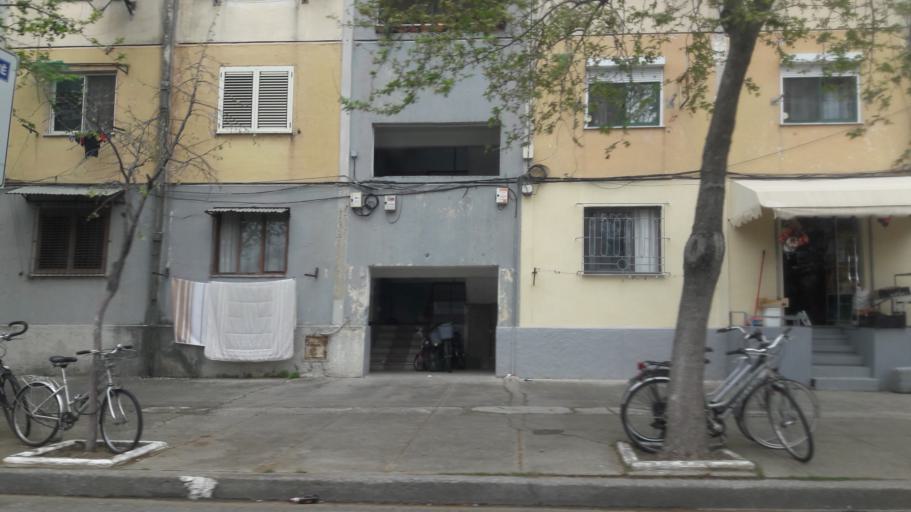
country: AL
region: Shkoder
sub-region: Rrethi i Shkodres
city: Shkoder
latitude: 42.0580
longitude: 19.5047
